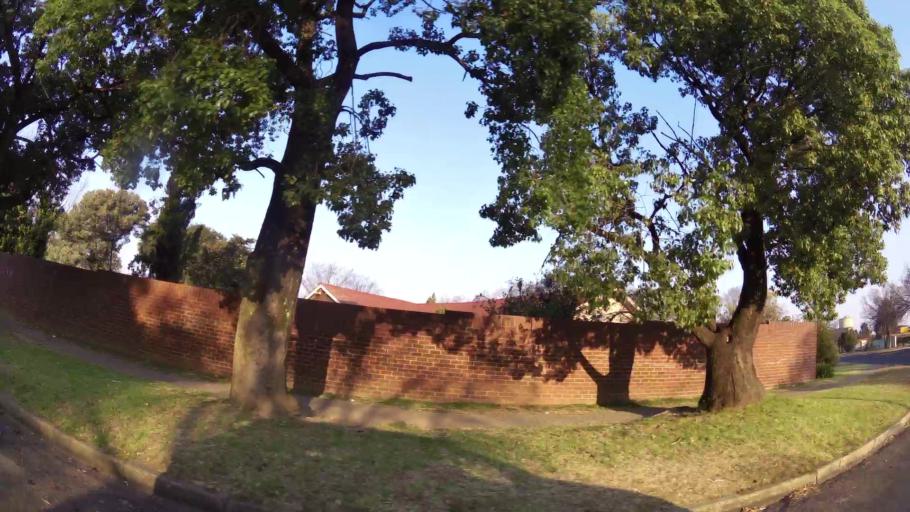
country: ZA
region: Gauteng
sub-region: Ekurhuleni Metropolitan Municipality
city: Springs
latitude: -26.3031
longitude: 28.4481
